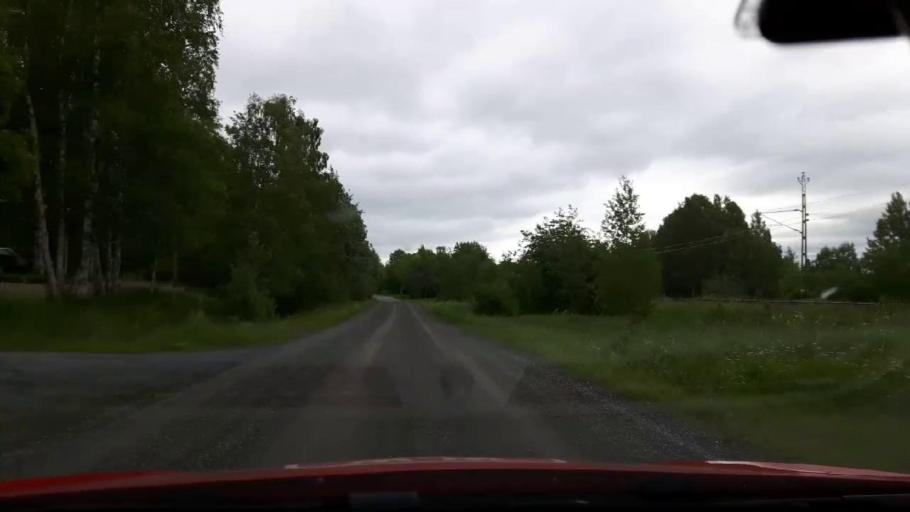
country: SE
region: Jaemtland
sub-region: Krokoms Kommun
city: Krokom
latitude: 63.2468
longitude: 14.5294
